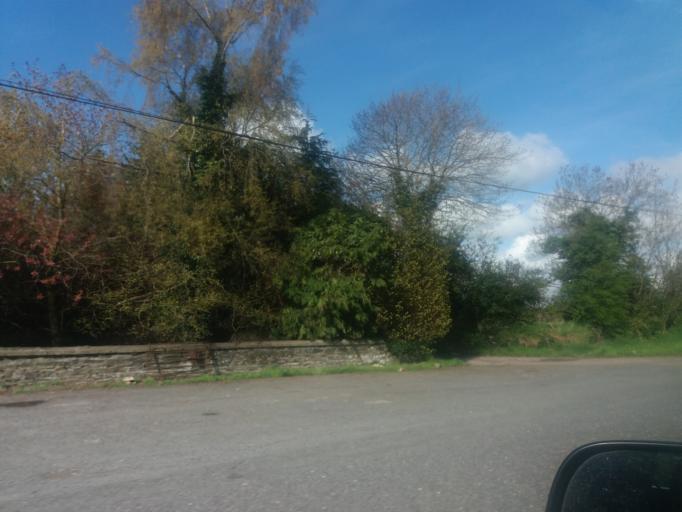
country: IE
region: Ulster
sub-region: An Cabhan
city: Mullagh
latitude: 53.7863
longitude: -7.0192
